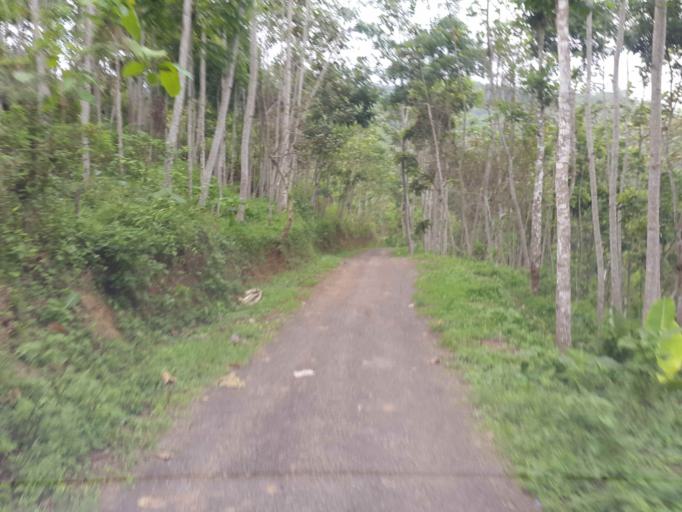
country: ID
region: Central Java
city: Jambuluwuk
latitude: -7.3304
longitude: 108.9423
